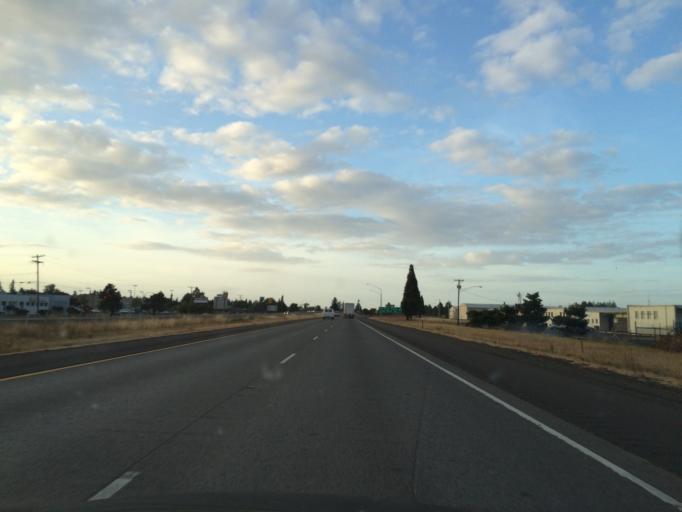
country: US
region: Oregon
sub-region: Linn County
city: Albany
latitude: 44.6368
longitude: -123.0622
